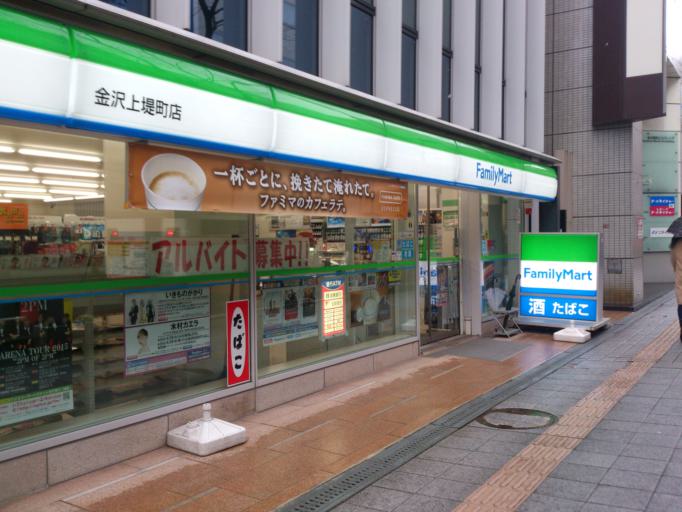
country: JP
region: Ishikawa
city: Kanazawa-shi
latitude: 36.5685
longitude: 136.6542
